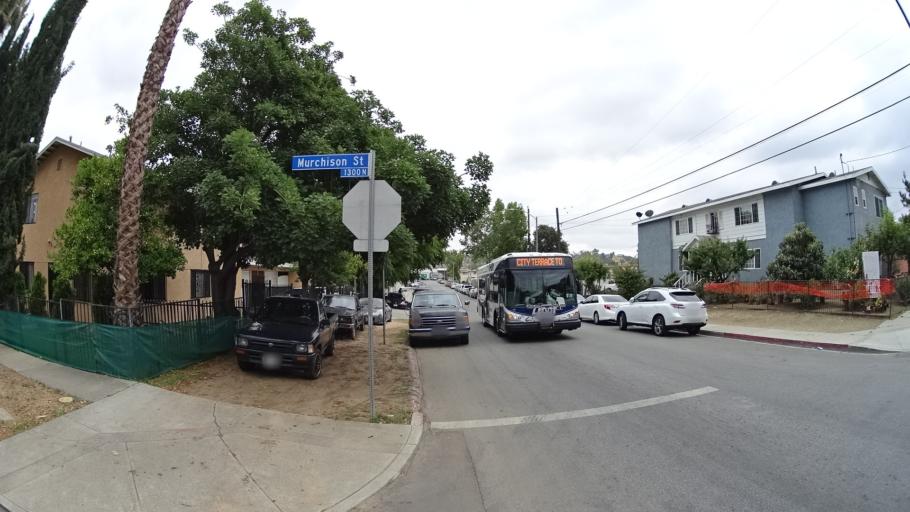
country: US
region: California
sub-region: Los Angeles County
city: Boyle Heights
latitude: 34.0610
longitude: -118.1948
